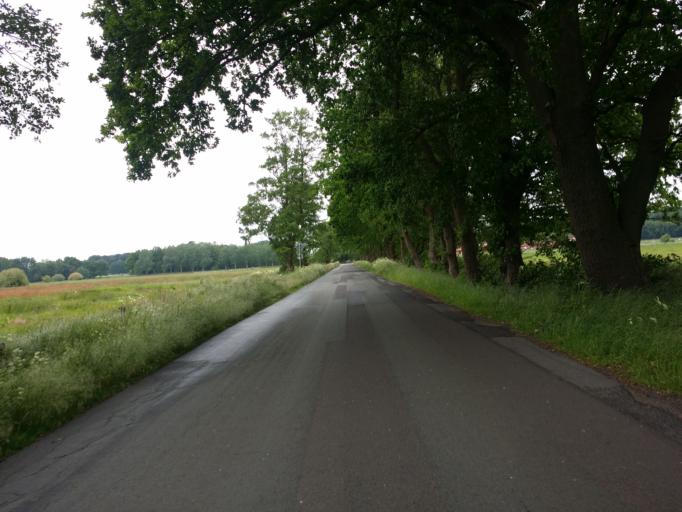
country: DE
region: Lower Saxony
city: Delmenhorst
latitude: 53.0276
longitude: 8.5918
